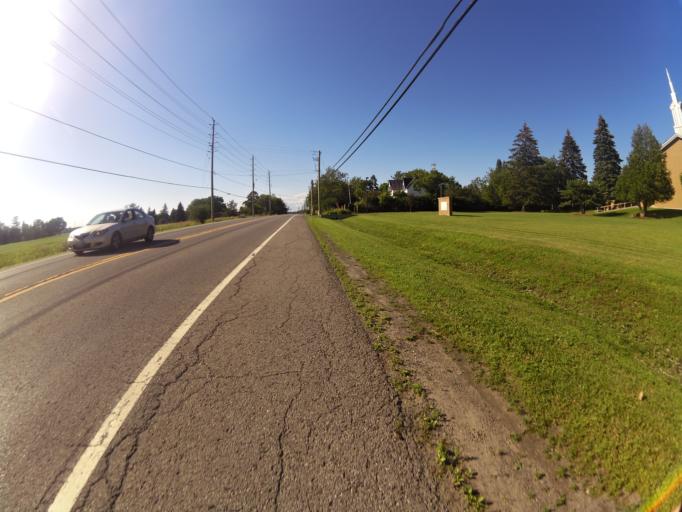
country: CA
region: Ontario
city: Bells Corners
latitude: 45.2723
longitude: -75.8325
